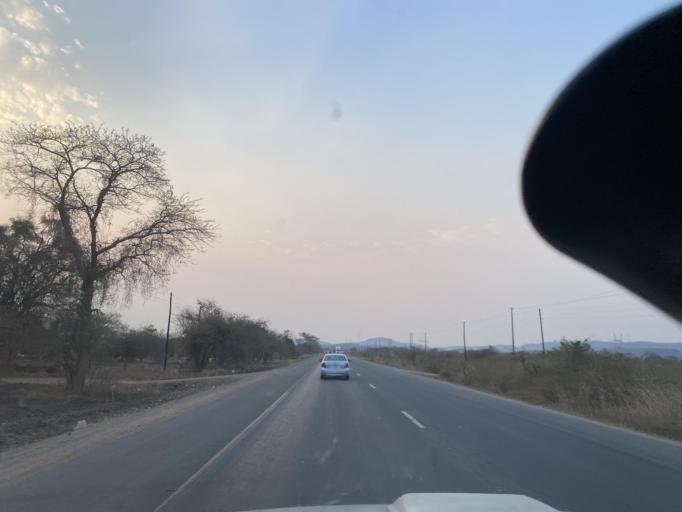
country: ZM
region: Lusaka
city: Kafue
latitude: -15.8315
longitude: 28.2337
